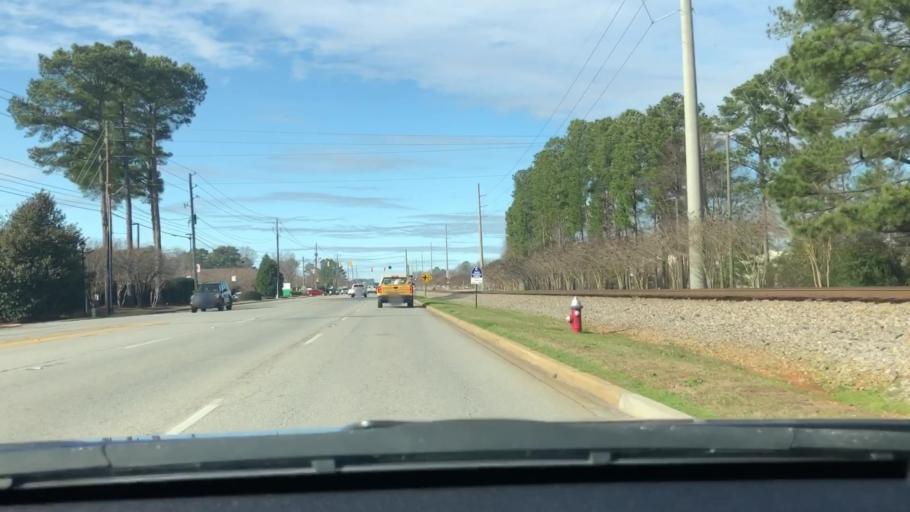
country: US
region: South Carolina
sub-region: Lexington County
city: Irmo
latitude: 34.0767
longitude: -81.1780
